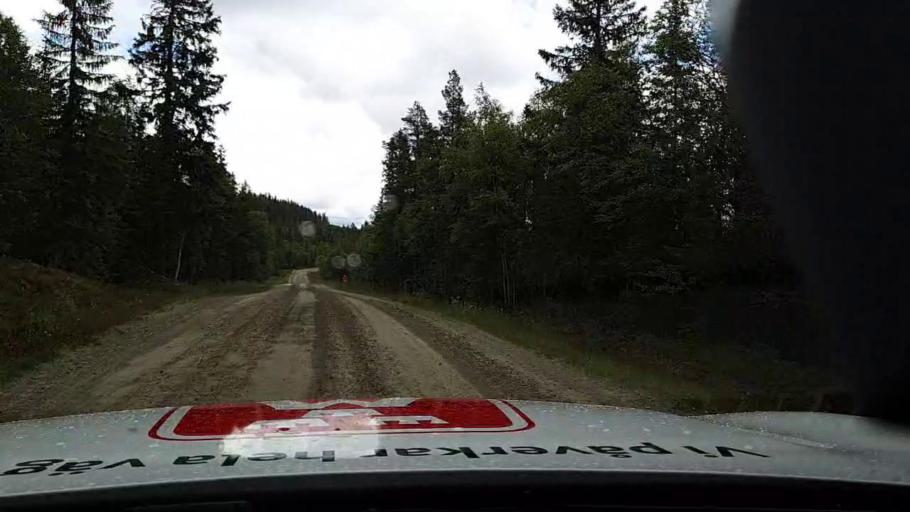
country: SE
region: Jaemtland
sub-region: Are Kommun
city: Jarpen
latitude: 62.6067
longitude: 13.2125
